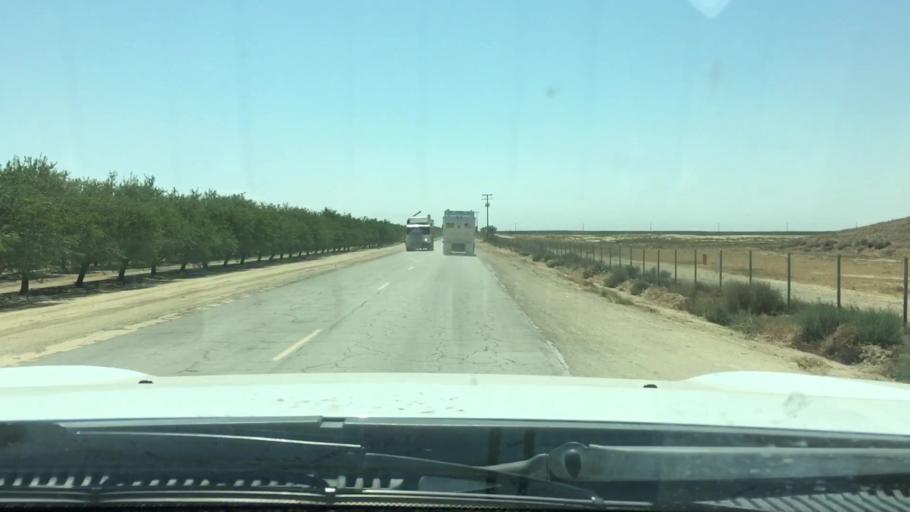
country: US
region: California
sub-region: Kern County
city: Wasco
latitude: 35.5132
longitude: -119.4033
